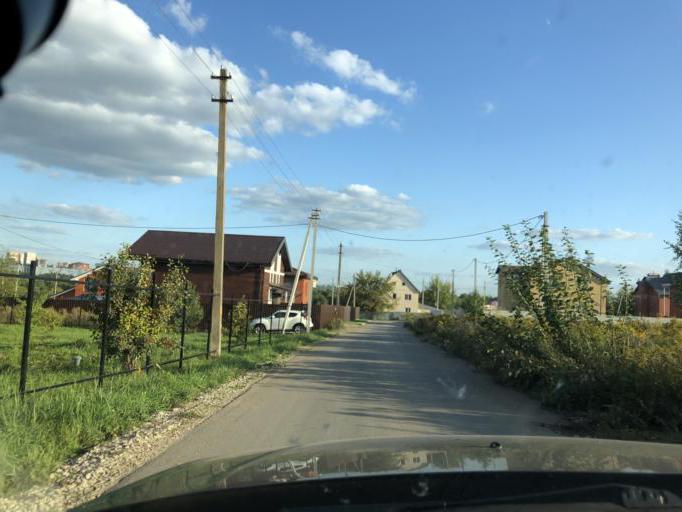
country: RU
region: Tula
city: Kosaya Gora
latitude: 54.1747
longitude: 37.5451
